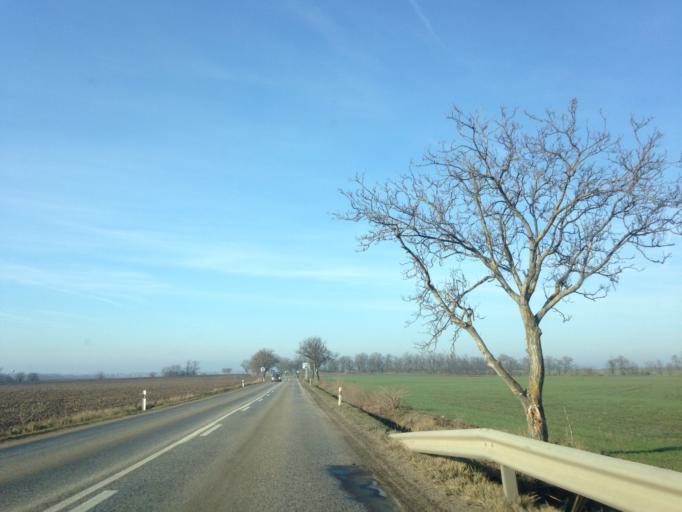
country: SK
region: Nitriansky
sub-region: Okres Nove Zamky
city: Nove Zamky
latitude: 47.9915
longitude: 18.3204
